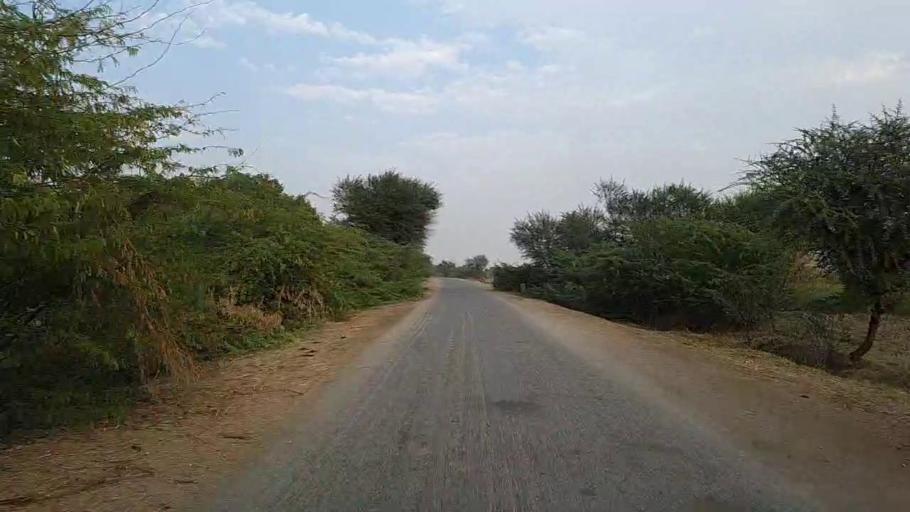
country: PK
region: Sindh
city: Samaro
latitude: 25.3824
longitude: 69.3410
